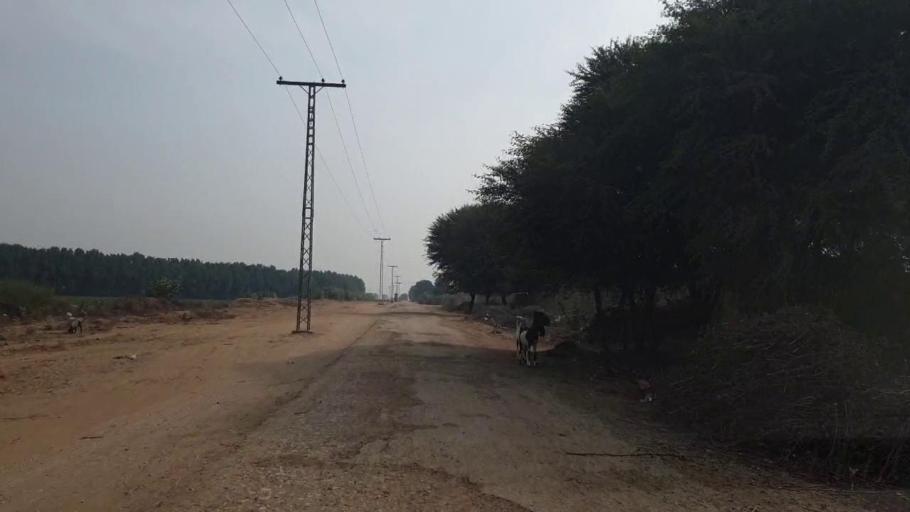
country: PK
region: Sindh
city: Sann
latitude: 26.0308
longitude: 68.1369
